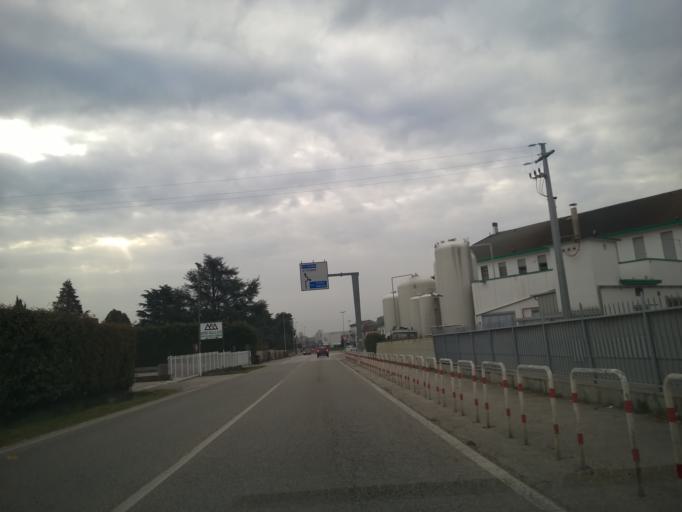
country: IT
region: Veneto
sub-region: Provincia di Vicenza
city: Zane
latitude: 45.7190
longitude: 11.4542
